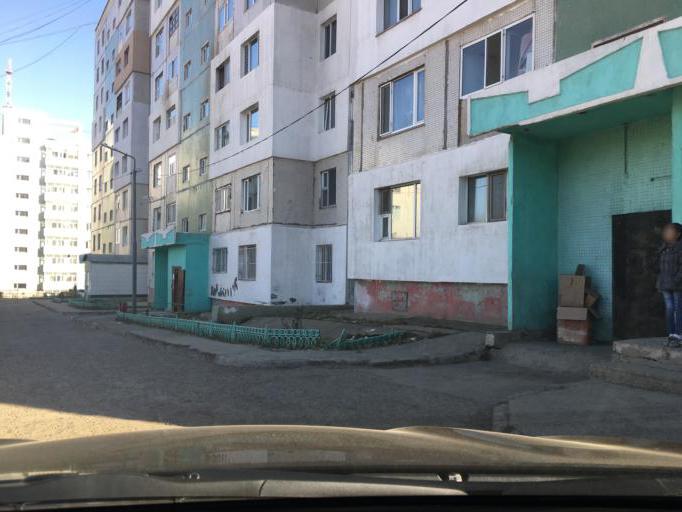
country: MN
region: Ulaanbaatar
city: Ulaanbaatar
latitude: 47.9281
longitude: 106.8801
